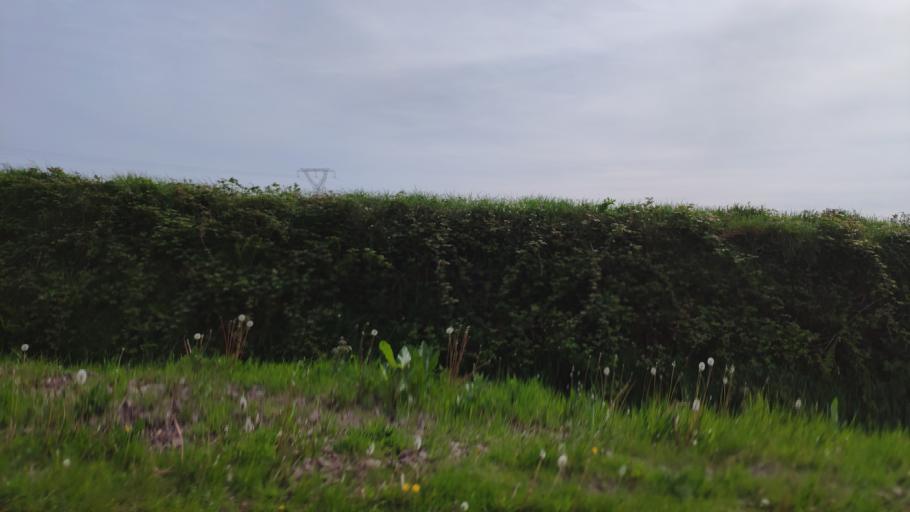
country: IE
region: Munster
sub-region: County Cork
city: Blarney
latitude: 51.9740
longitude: -8.5130
